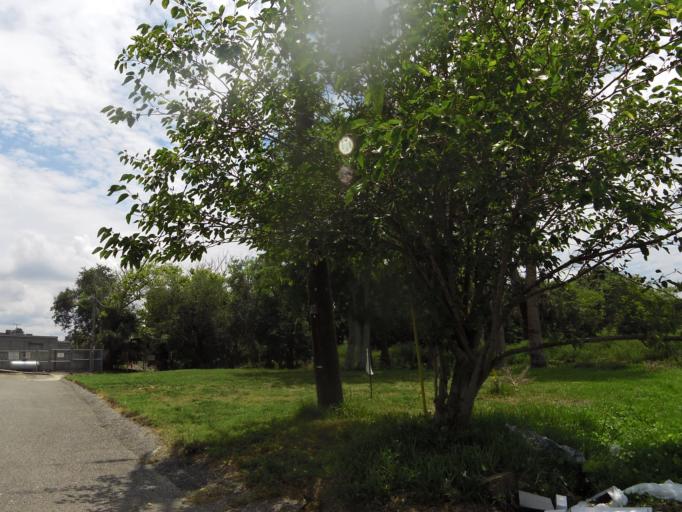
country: US
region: Florida
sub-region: Duval County
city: Atlantic Beach
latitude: 30.3271
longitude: -81.4122
